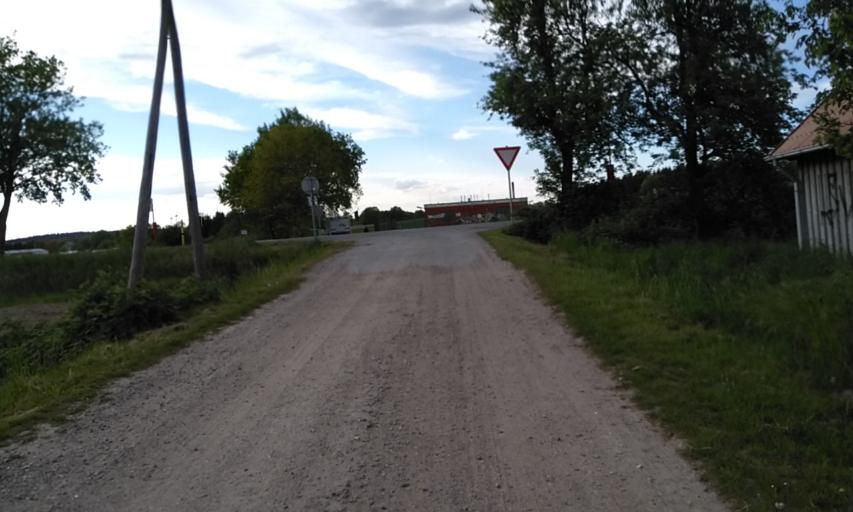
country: DE
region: Lower Saxony
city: Harsefeld
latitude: 53.4595
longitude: 9.5308
